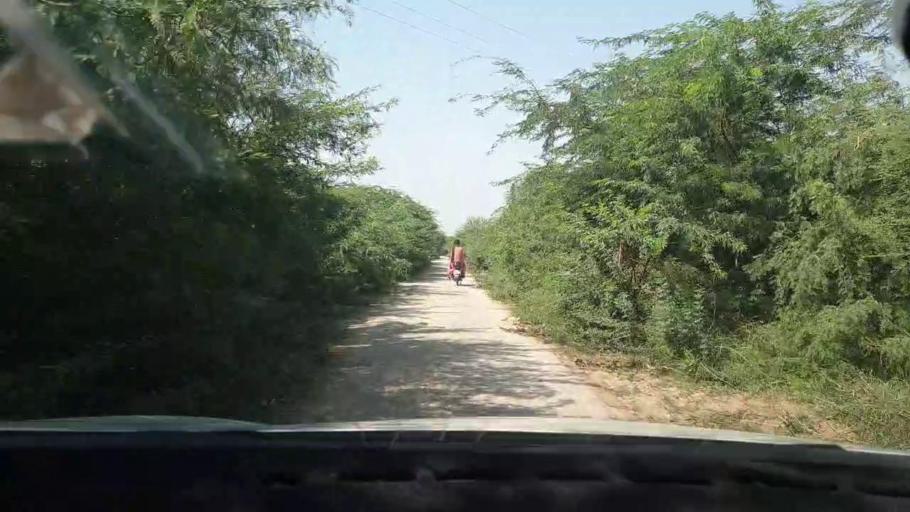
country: PK
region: Sindh
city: Tando Mittha Khan
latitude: 25.8614
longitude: 69.3858
